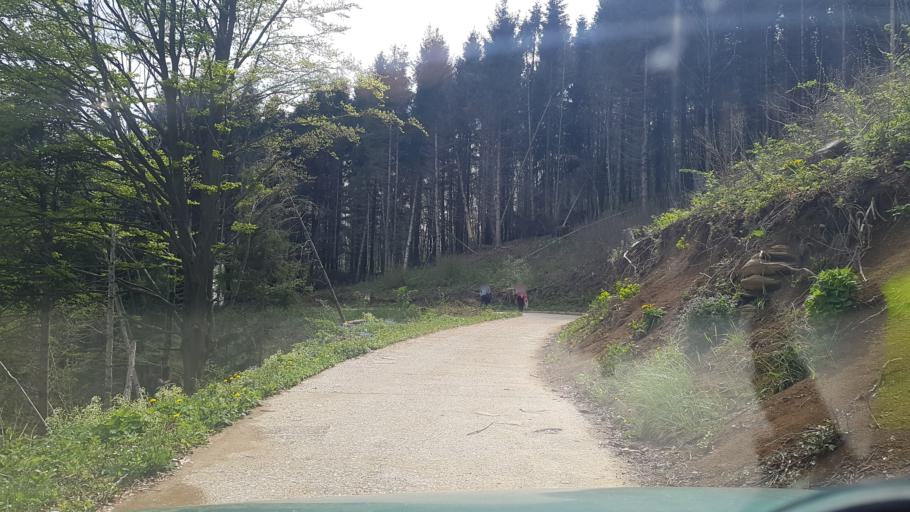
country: IT
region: Friuli Venezia Giulia
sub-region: Provincia di Udine
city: Faedis
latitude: 46.1872
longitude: 13.3823
